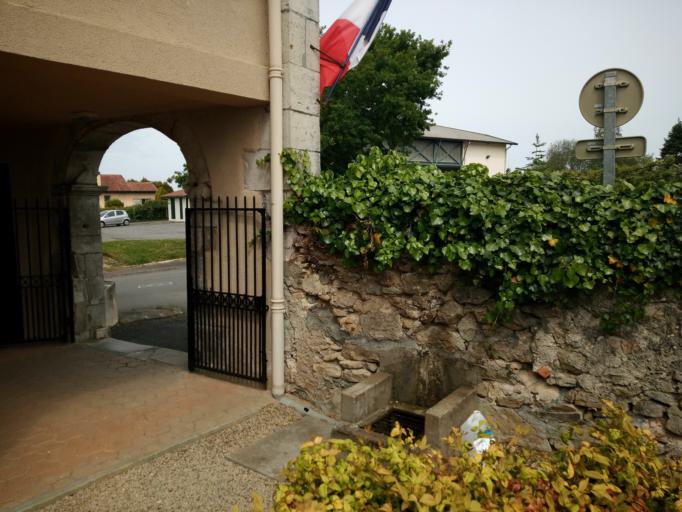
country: FR
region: Aquitaine
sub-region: Departement des Landes
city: Saint-Martin-de-Hinx
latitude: 43.5331
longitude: -1.2680
